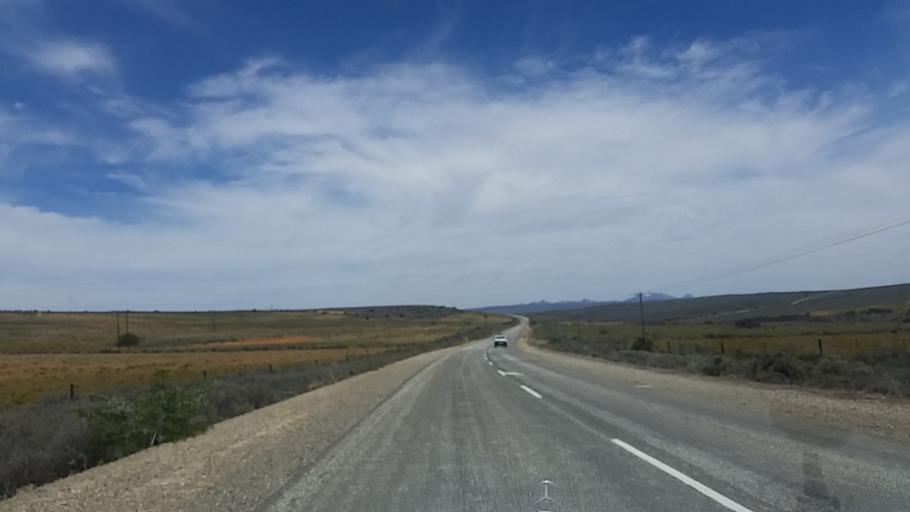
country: ZA
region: Western Cape
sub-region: Eden District Municipality
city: Knysna
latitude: -33.6213
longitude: 23.1385
